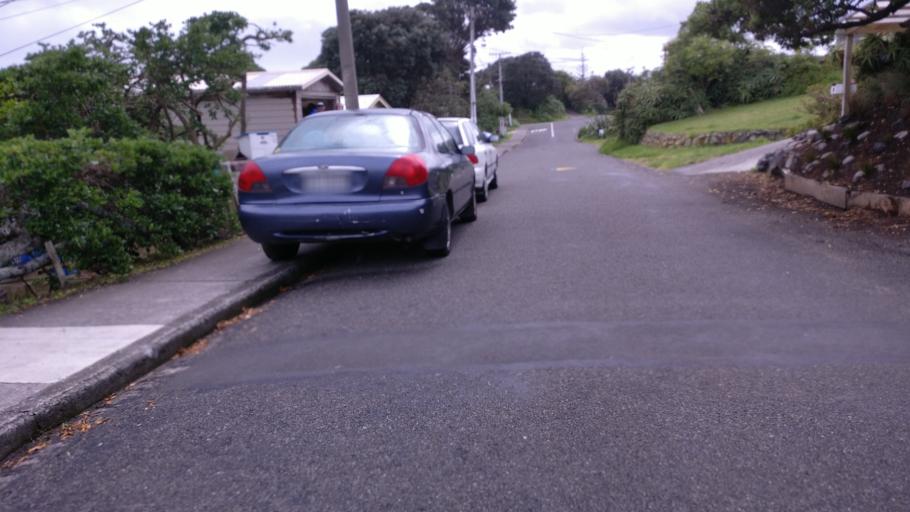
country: NZ
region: Wellington
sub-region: Kapiti Coast District
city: Paraparaumu
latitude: -40.9767
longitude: 174.9588
